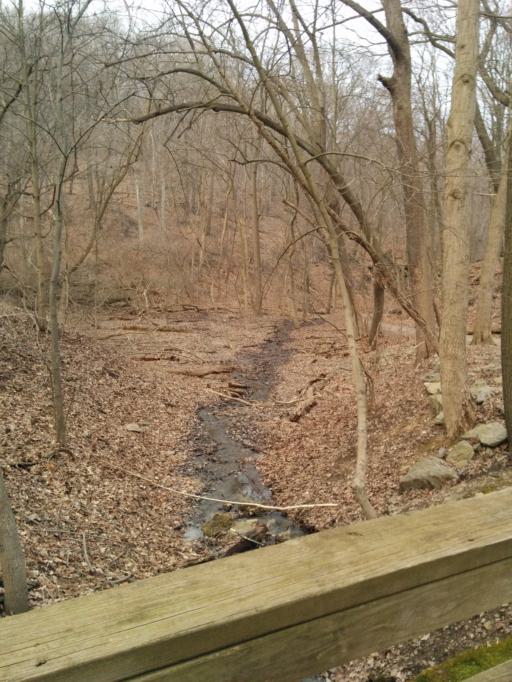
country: US
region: Pennsylvania
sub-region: Allegheny County
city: Edgewood
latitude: 40.4345
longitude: -79.9078
